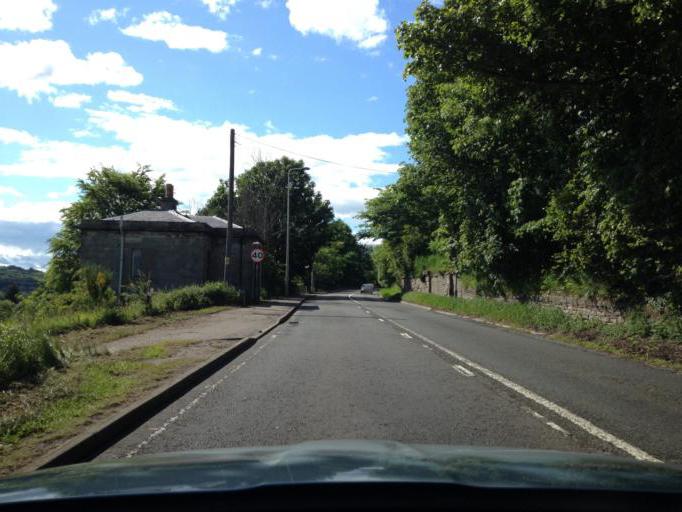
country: GB
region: Scotland
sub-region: Perth and Kinross
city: Perth
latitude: 56.3823
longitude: -3.4130
